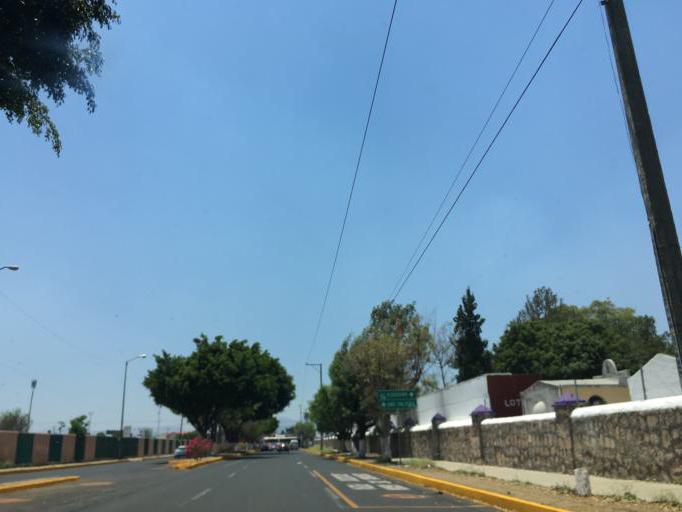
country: MX
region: Michoacan
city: Morelia
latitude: 19.6921
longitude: -101.2102
